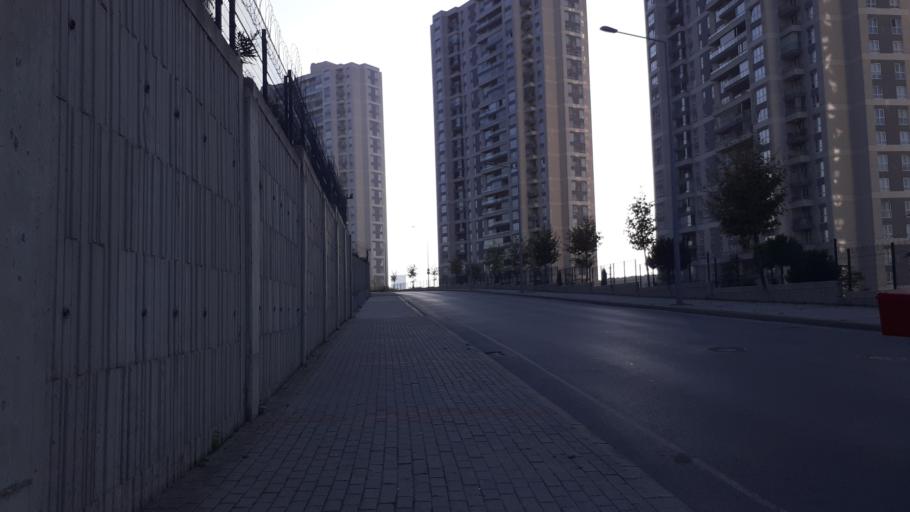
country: TR
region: Istanbul
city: Basaksehir
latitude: 41.0672
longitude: 28.7773
